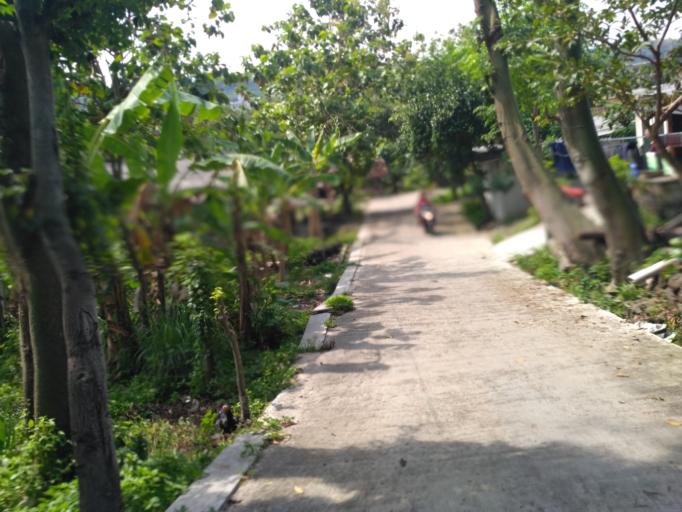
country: ID
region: Central Java
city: Semarang
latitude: -7.0398
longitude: 110.4405
